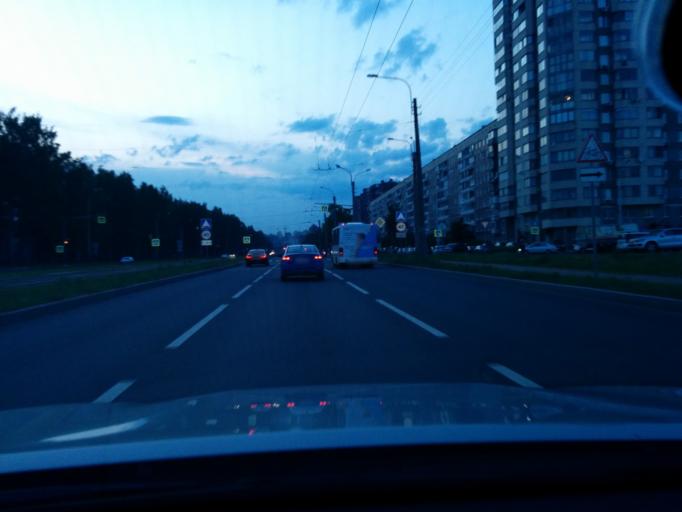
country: RU
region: St.-Petersburg
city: Sosnovka
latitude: 60.0219
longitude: 30.3671
